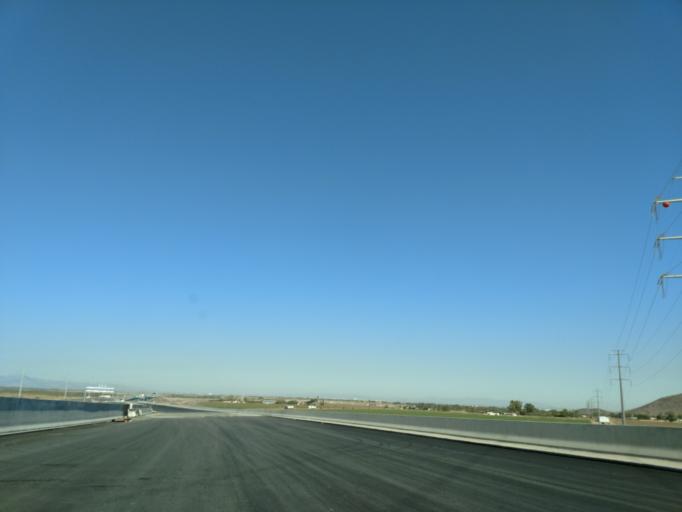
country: US
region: Arizona
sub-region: Maricopa County
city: Laveen
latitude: 33.3238
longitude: -112.1653
